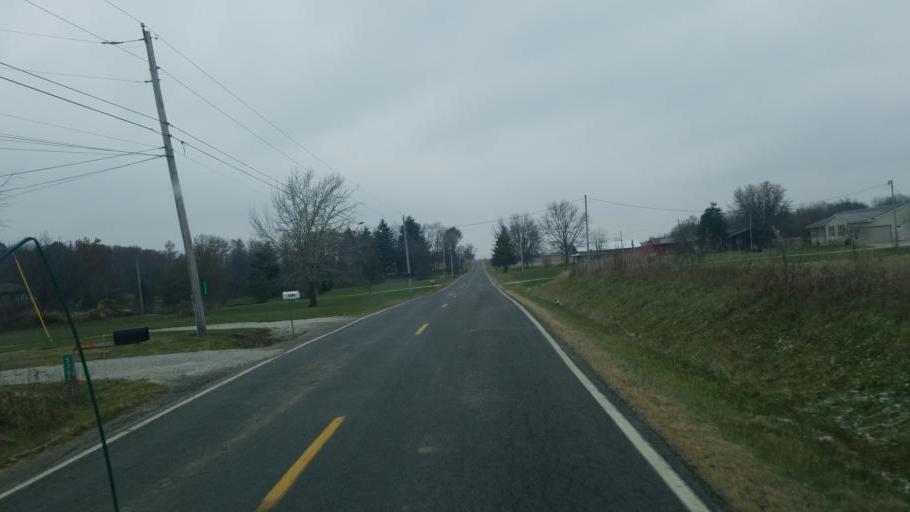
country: US
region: Ohio
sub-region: Medina County
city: Lodi
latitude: 41.1274
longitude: -82.0021
